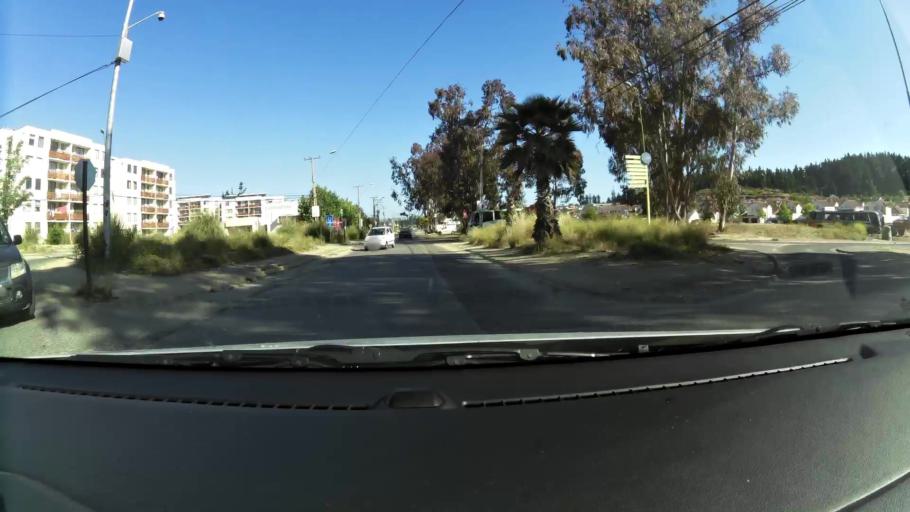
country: CL
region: Valparaiso
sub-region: Provincia de Valparaiso
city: Valparaiso
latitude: -33.1243
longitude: -71.5722
